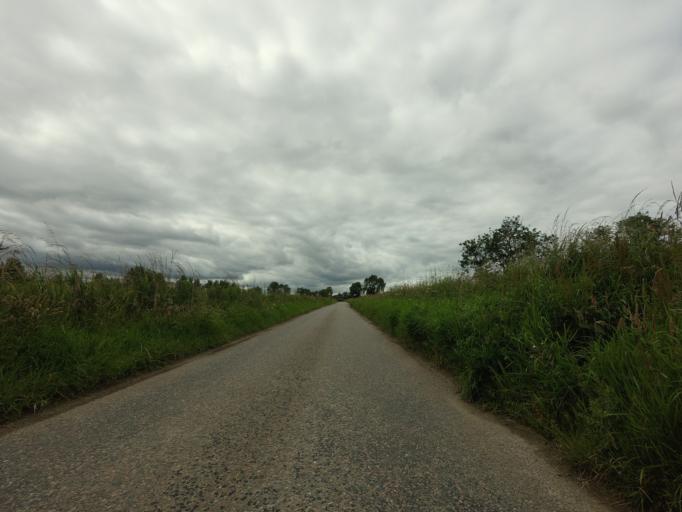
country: GB
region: Scotland
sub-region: Moray
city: Forres
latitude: 57.6175
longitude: -3.6188
